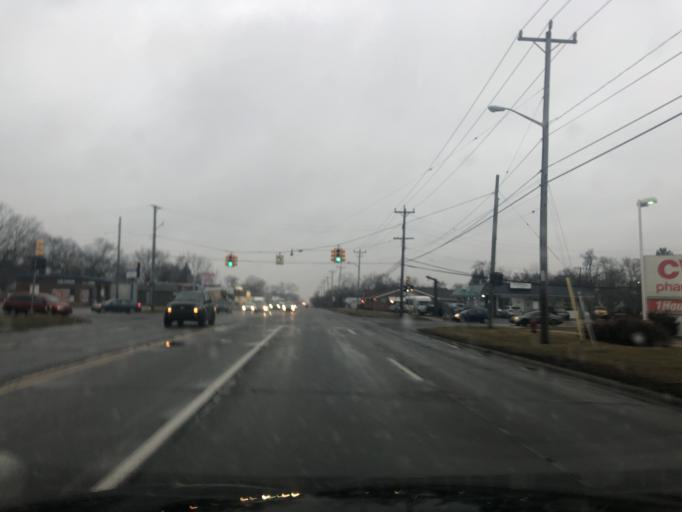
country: US
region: Michigan
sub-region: Wayne County
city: Inkster
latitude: 42.2687
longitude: -83.2887
